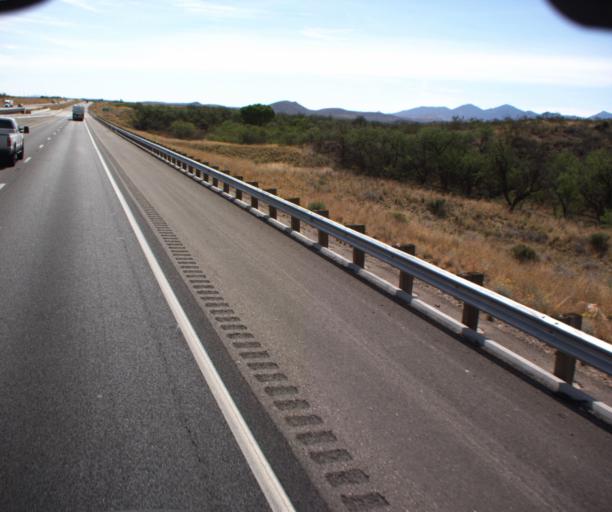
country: US
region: Arizona
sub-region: Cochise County
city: Mescal
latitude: 31.9860
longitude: -110.5698
